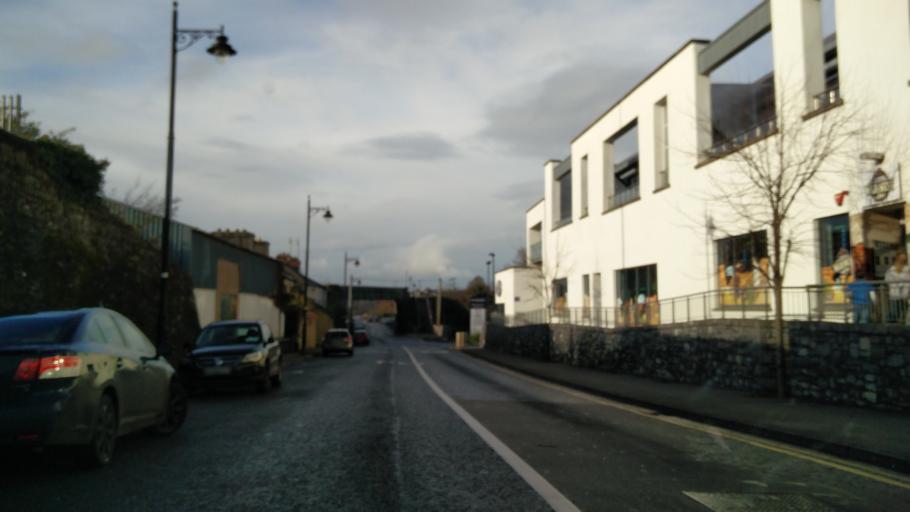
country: IE
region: Connaught
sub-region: Maigh Eo
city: Westport
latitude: 53.7970
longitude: -9.5115
